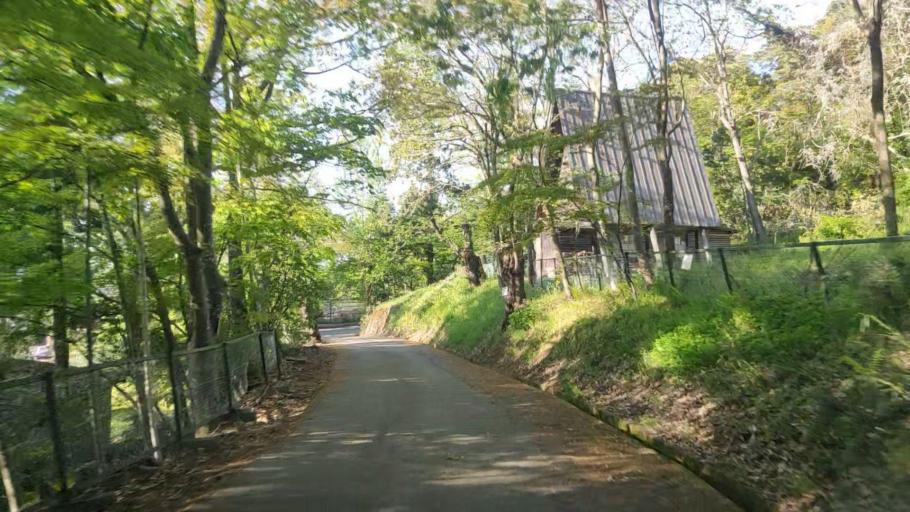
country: JP
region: Yamagata
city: Tendo
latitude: 38.3553
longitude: 140.3741
